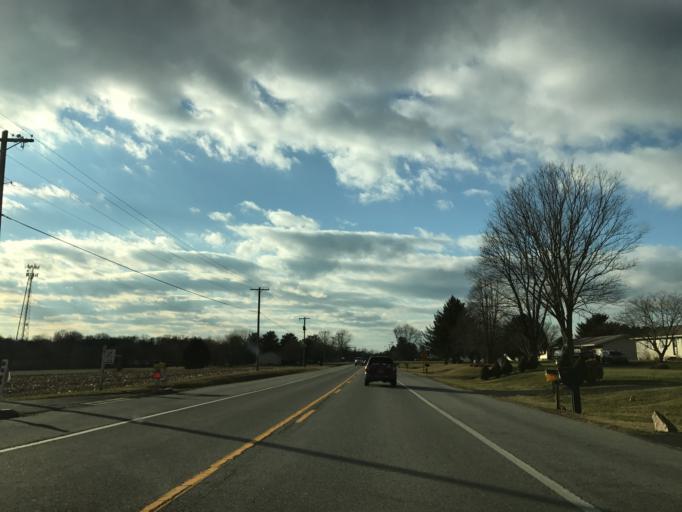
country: US
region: Maryland
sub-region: Cecil County
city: Rising Sun
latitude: 39.6922
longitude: -76.0527
